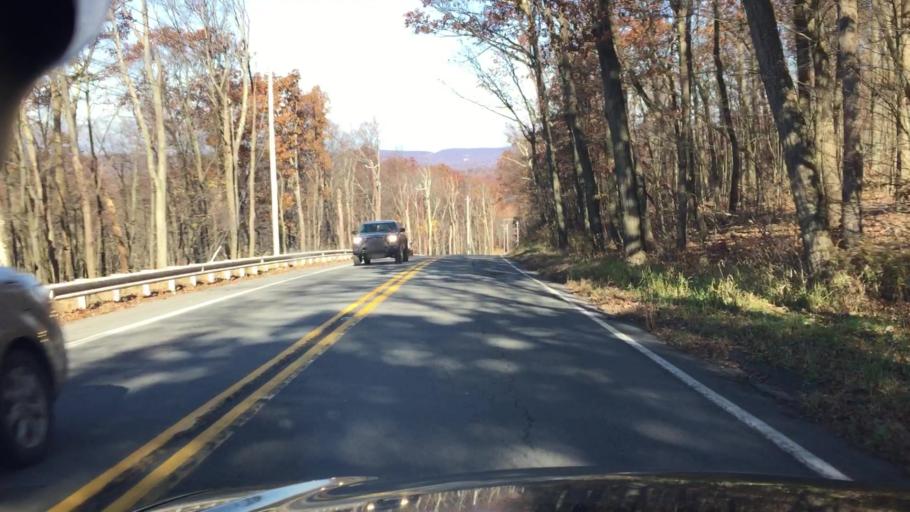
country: US
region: Pennsylvania
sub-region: Luzerne County
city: Freeland
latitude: 41.0777
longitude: -75.9584
